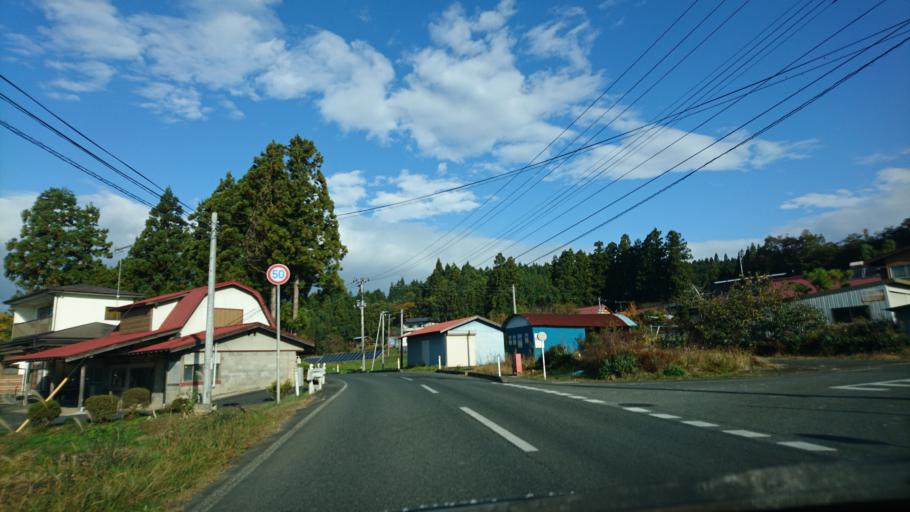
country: JP
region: Iwate
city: Mizusawa
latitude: 39.0330
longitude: 141.0783
